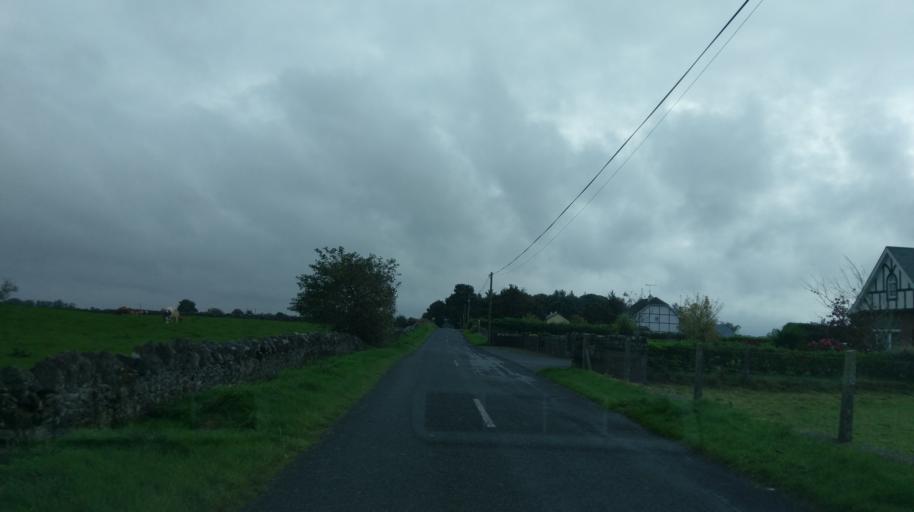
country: IE
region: Connaught
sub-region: County Galway
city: Athenry
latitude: 53.4570
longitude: -8.6062
